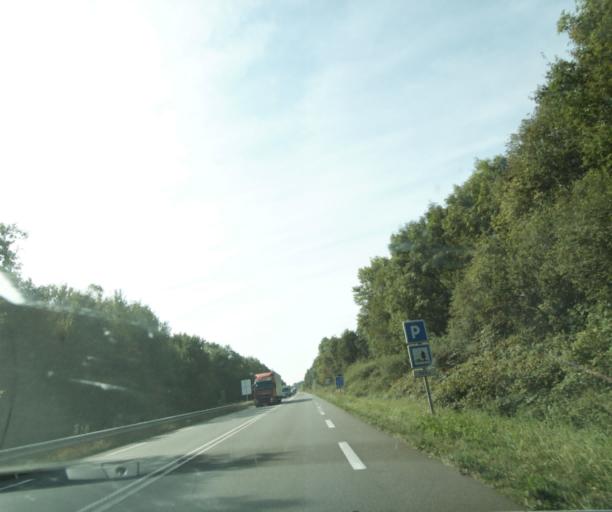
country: FR
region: Bourgogne
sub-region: Departement de Saone-et-Loire
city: Palinges
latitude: 46.5289
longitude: 4.1666
